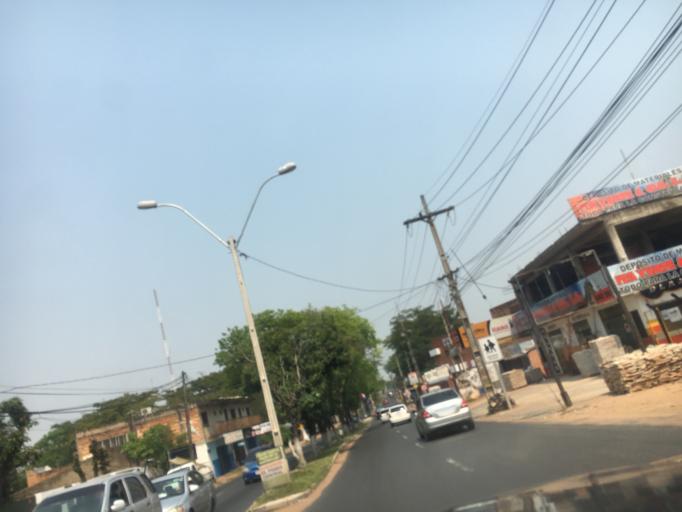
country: PY
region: Central
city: Villa Elisa
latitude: -25.3772
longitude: -57.5848
